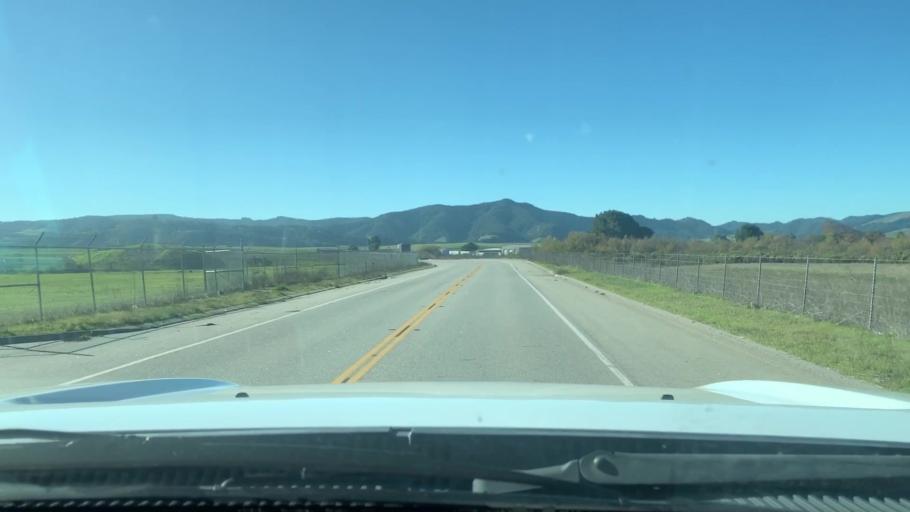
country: US
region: California
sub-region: San Luis Obispo County
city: San Luis Obispo
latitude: 35.2429
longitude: -120.6506
